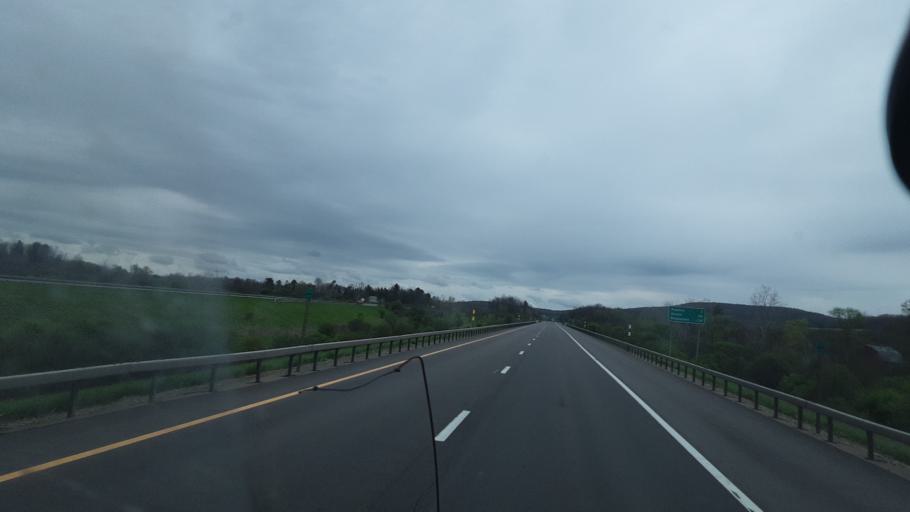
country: US
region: New York
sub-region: Allegany County
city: Belmont
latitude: 42.2679
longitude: -78.0540
